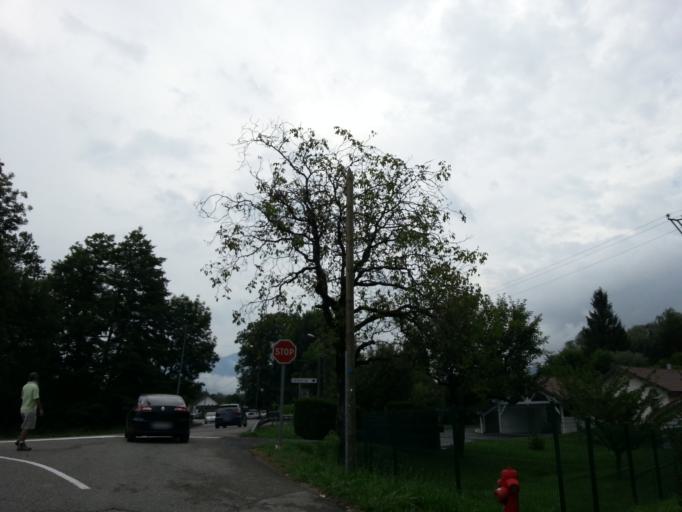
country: FR
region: Rhone-Alpes
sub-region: Departement de la Haute-Savoie
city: Doussard
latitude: 45.7933
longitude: 6.2132
